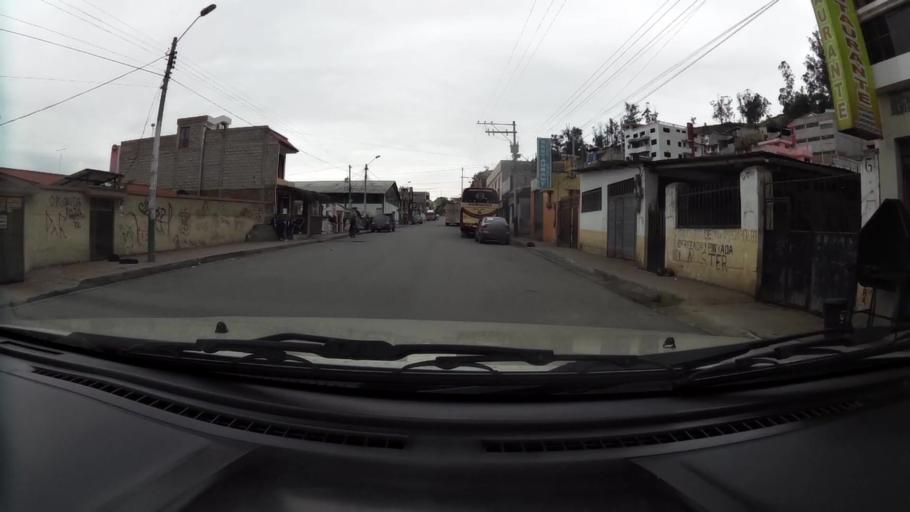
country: EC
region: Chimborazo
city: Alausi
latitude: -2.2888
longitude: -78.9196
